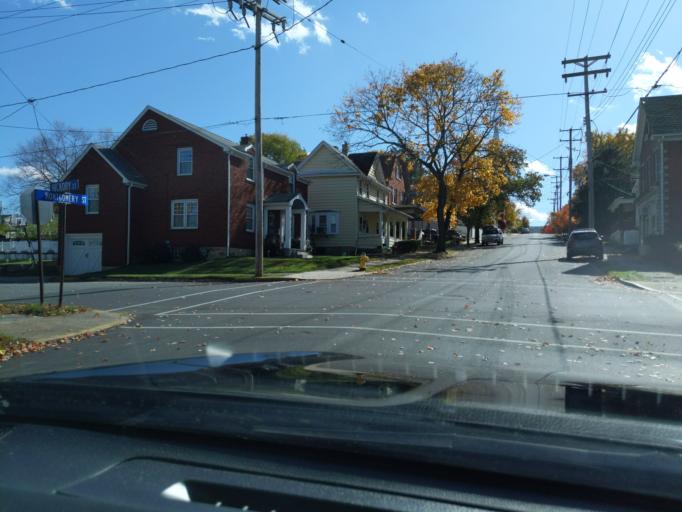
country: US
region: Pennsylvania
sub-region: Blair County
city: Hollidaysburg
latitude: 40.4326
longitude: -78.3973
